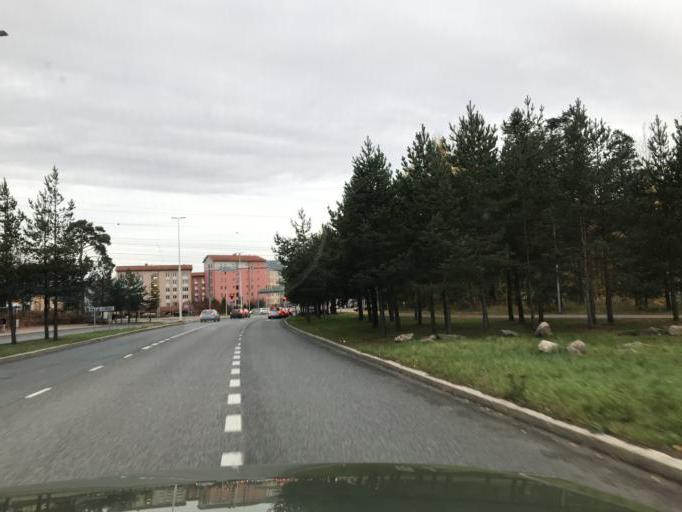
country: FI
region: Uusimaa
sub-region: Helsinki
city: Vantaa
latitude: 60.2910
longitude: 24.9603
